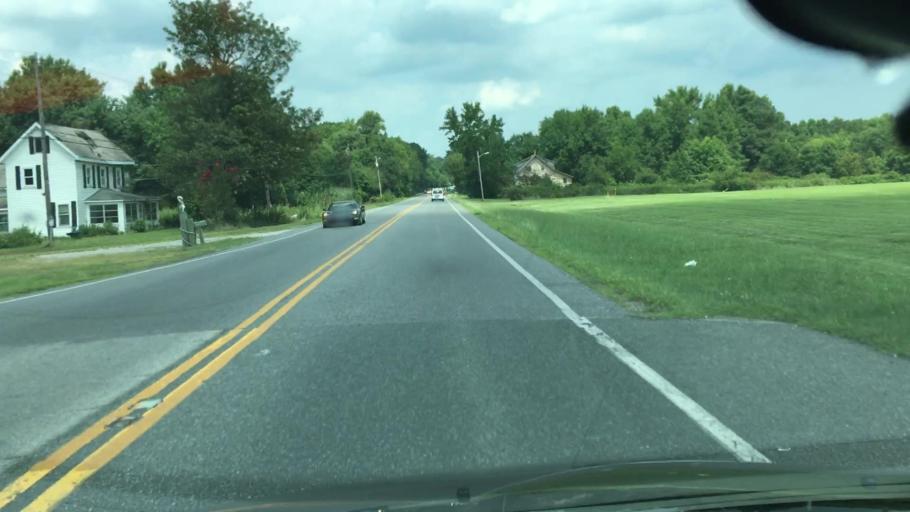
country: US
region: Maryland
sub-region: Worcester County
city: Ocean Pines
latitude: 38.3544
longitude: -75.1687
